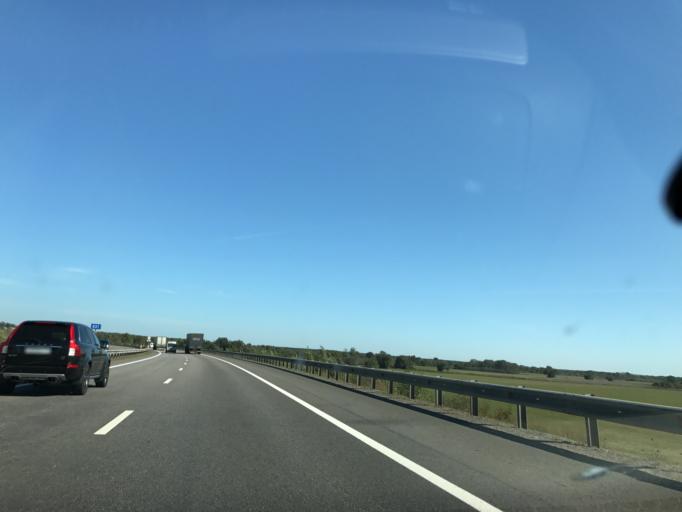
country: RU
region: Voronezj
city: Verkhniy Mamon
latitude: 50.1590
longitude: 40.4296
